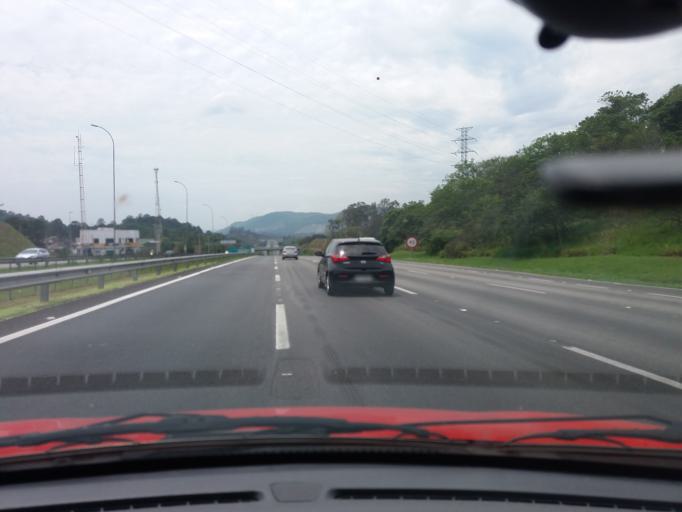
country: BR
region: Sao Paulo
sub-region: Caieiras
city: Caieiras
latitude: -23.4426
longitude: -46.7745
